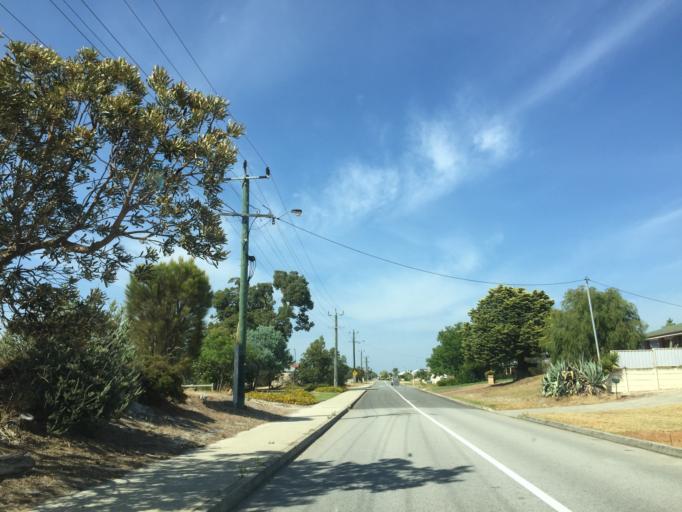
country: AU
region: Western Australia
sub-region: Gosnells
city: Thornlie
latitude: -32.0829
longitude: 115.9595
